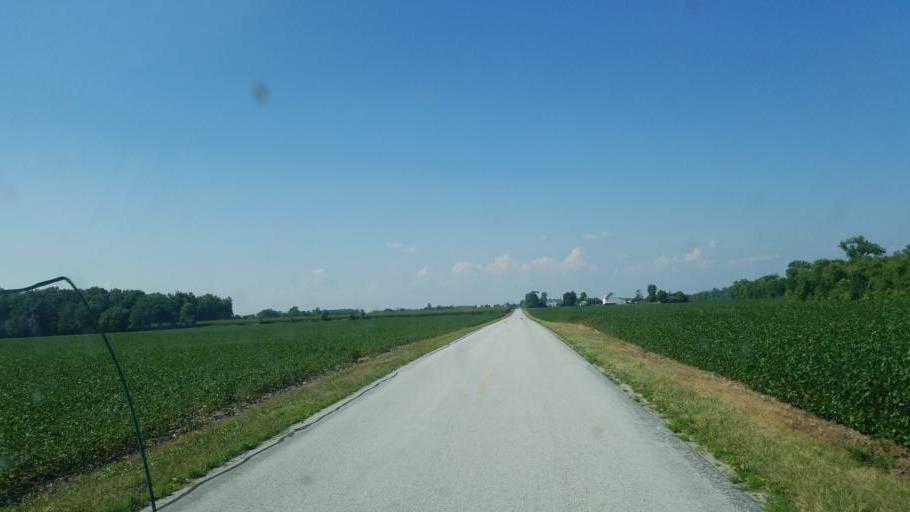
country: US
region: Ohio
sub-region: Hardin County
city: Forest
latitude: 40.6904
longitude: -83.4957
